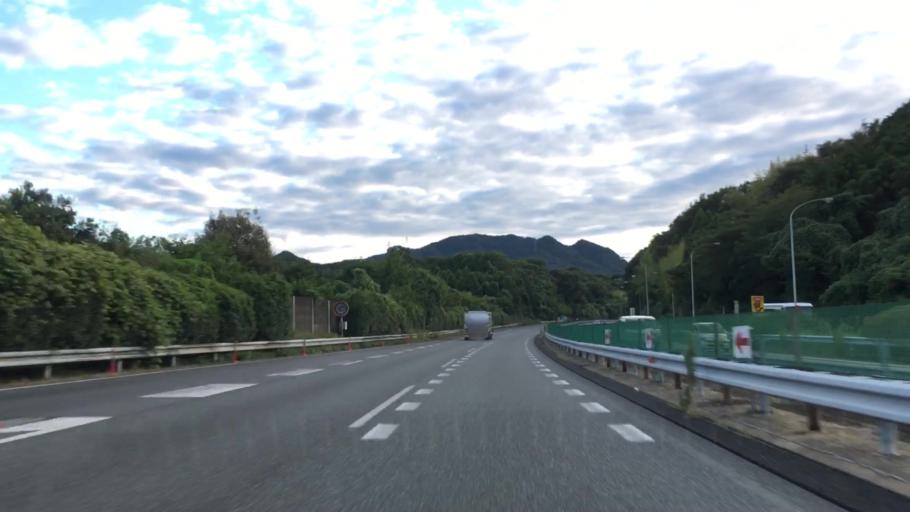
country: JP
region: Yamaguchi
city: Shimonoseki
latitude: 34.0493
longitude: 131.0032
